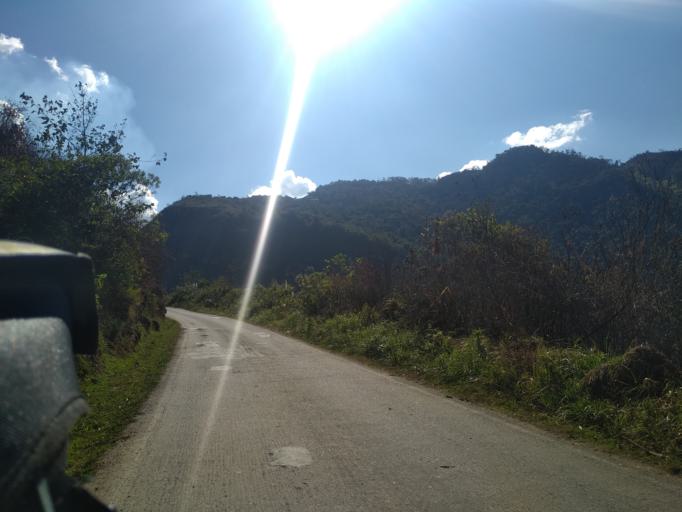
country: PE
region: Amazonas
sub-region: Provincia de Chachapoyas
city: Montevideo
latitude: -6.7132
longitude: -77.8178
